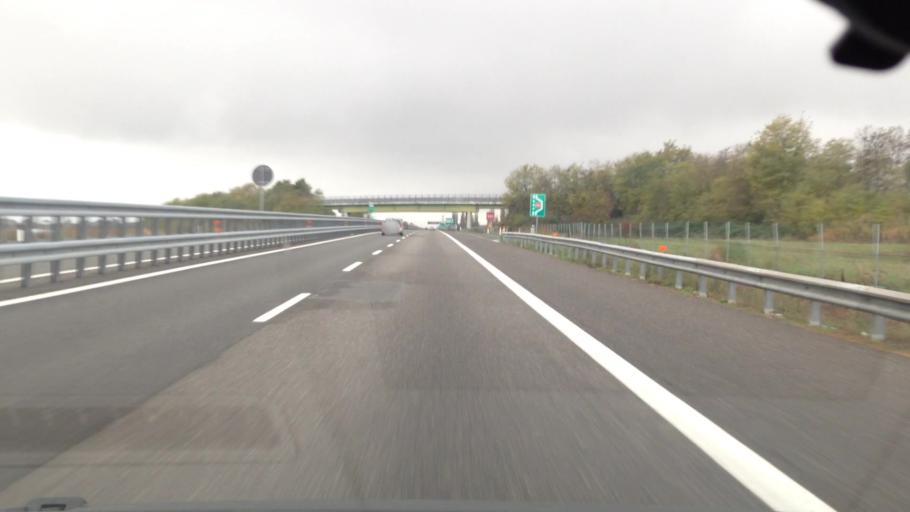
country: IT
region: Piedmont
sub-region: Provincia di Asti
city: San Paolo Solbrito
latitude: 44.9486
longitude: 7.9642
